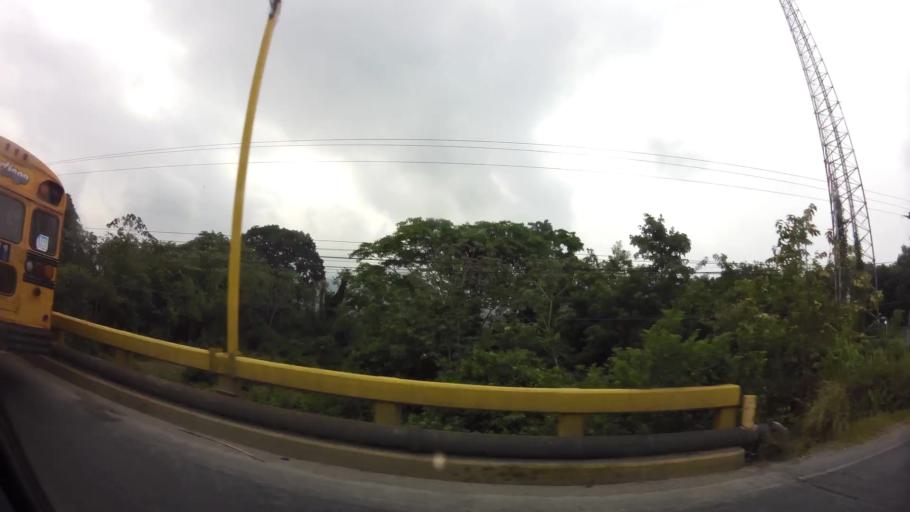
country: HN
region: Yoro
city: El Progreso
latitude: 15.4400
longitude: -87.7925
